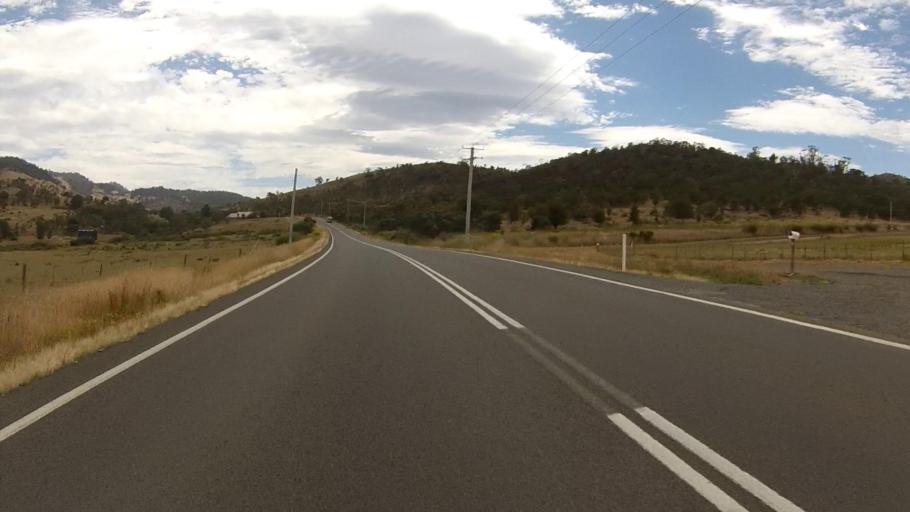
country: AU
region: Tasmania
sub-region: Brighton
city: Old Beach
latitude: -42.6881
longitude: 147.3511
